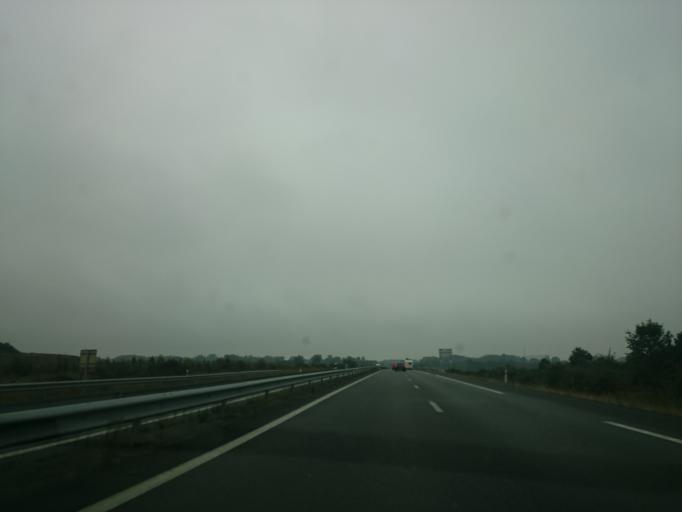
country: FR
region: Brittany
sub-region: Departement d'Ille-et-Vilaine
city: La Dominelais
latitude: 47.7627
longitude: -1.7113
